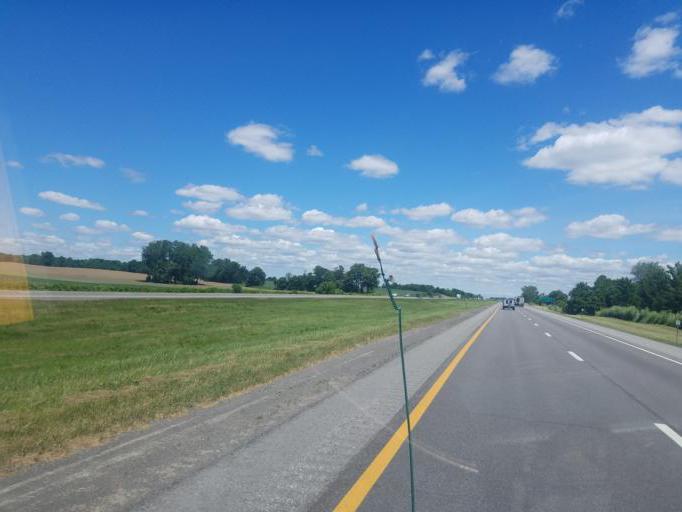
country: US
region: New York
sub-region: Genesee County
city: Batavia
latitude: 43.0171
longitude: -78.2161
